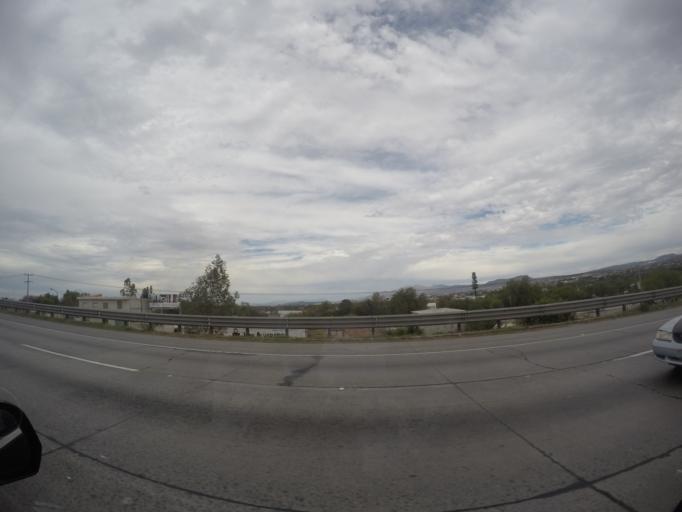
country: MX
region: Queretaro
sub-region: San Juan del Rio
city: Vista Hermosa (Cuasinada)
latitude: 20.3827
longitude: -100.0145
